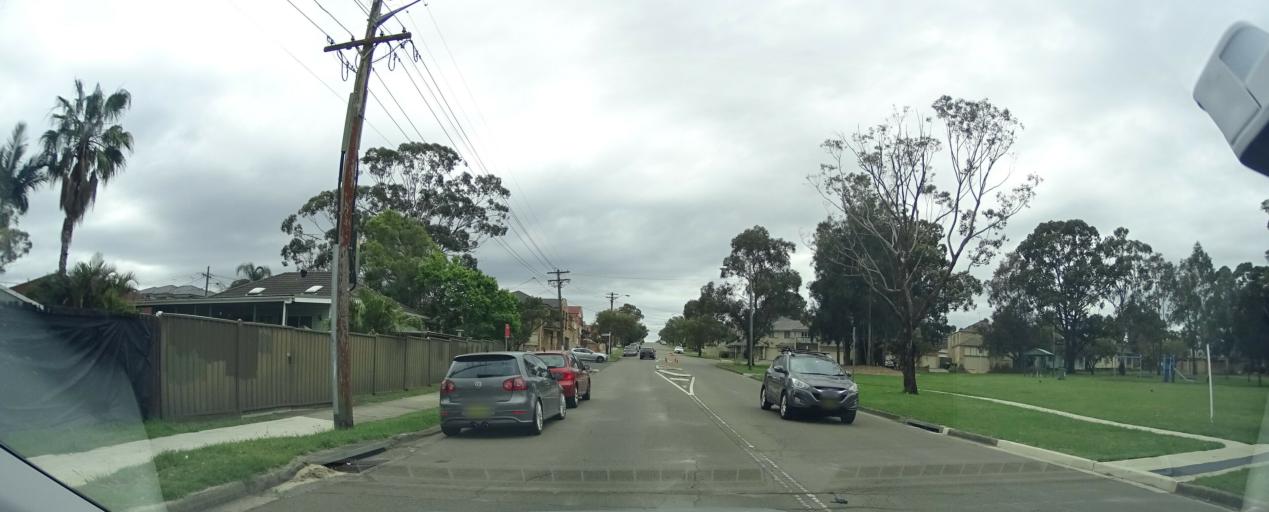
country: AU
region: New South Wales
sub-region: Bankstown
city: Padstow
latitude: -33.9563
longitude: 151.0250
